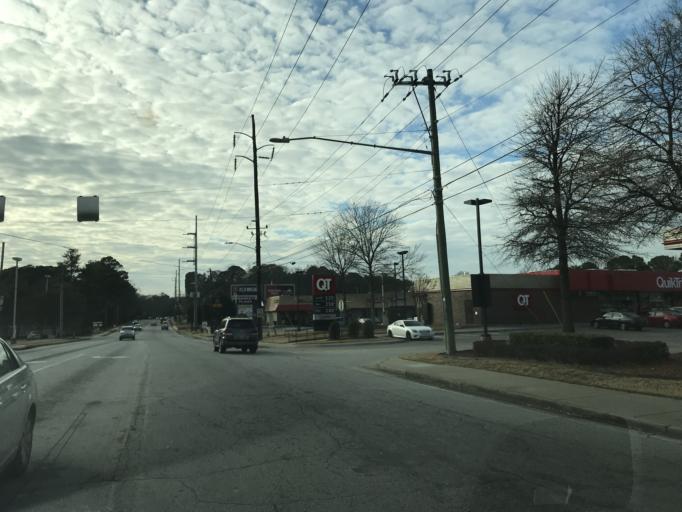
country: US
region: Georgia
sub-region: DeKalb County
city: Tucker
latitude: 33.8807
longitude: -84.2195
